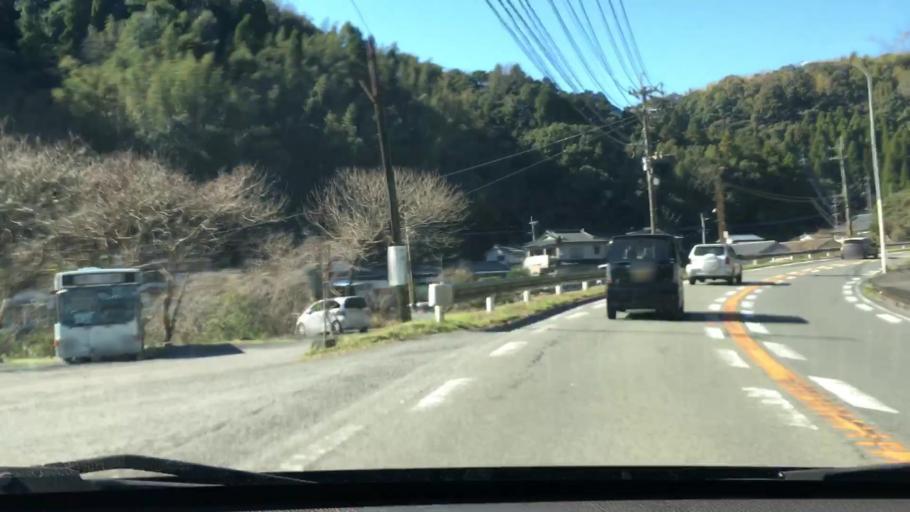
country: JP
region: Kagoshima
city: Kagoshima-shi
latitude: 31.6517
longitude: 130.5089
